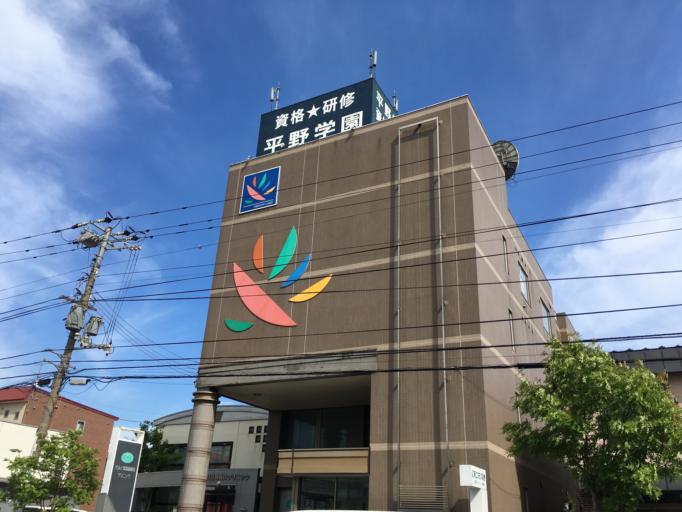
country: JP
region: Hokkaido
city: Muroran
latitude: 42.3476
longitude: 141.0252
